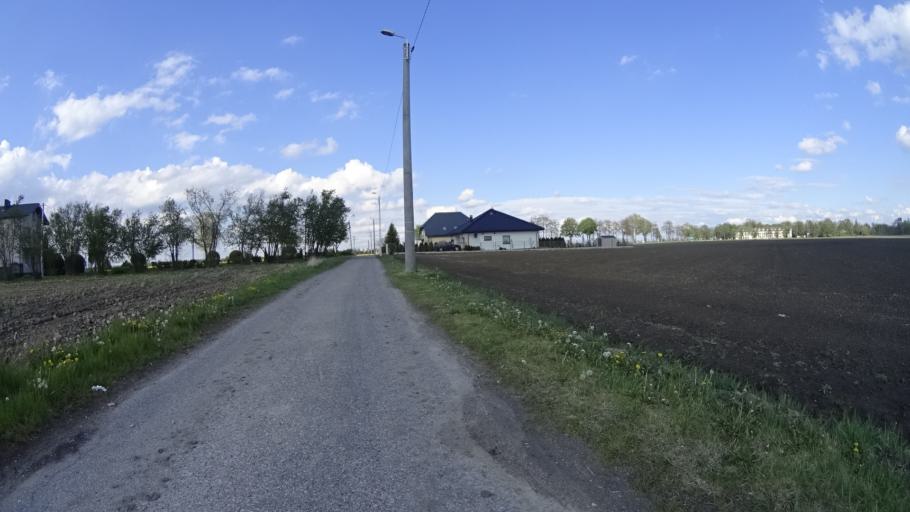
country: PL
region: Masovian Voivodeship
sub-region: Powiat warszawski zachodni
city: Jozefow
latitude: 52.2318
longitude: 20.6844
